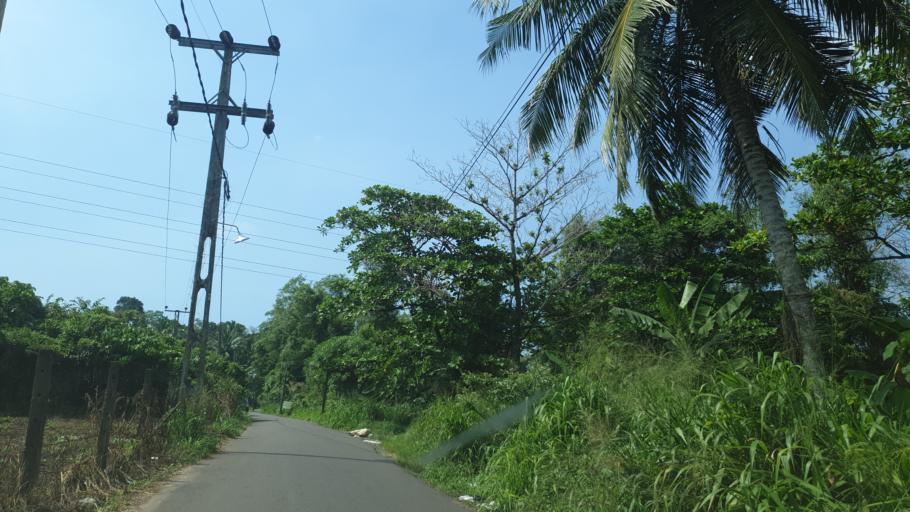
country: LK
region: Western
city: Panadura
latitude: 6.7416
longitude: 79.9480
